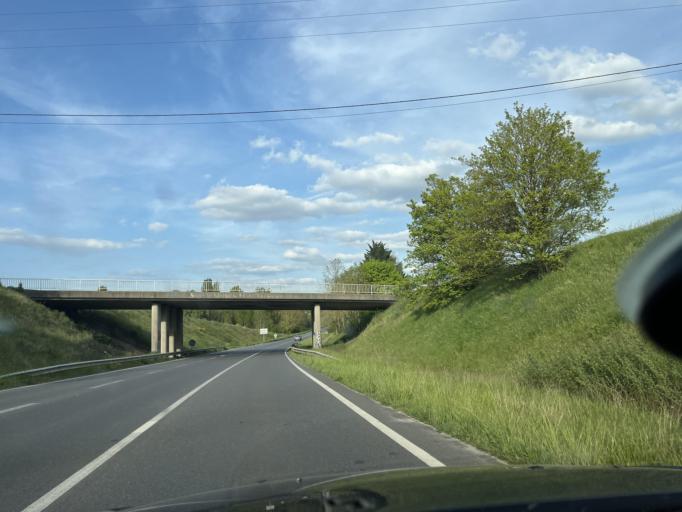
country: FR
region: Ile-de-France
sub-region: Departement de l'Essonne
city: Bruyeres-le-Chatel
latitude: 48.5866
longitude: 2.1898
